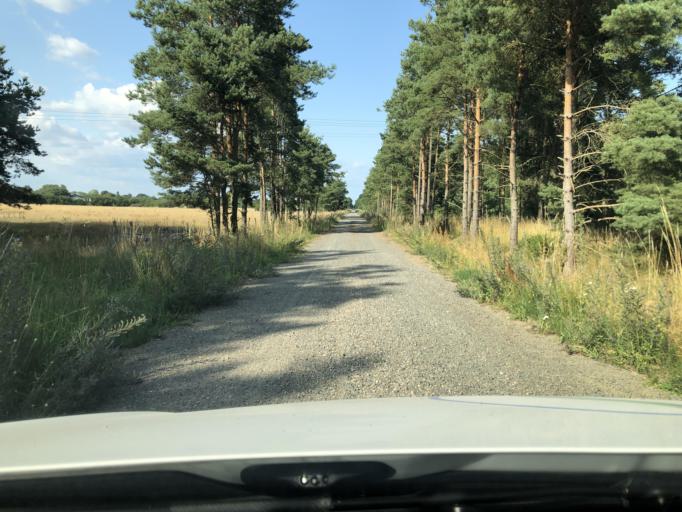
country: SE
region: Skane
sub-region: Kristianstads Kommun
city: Norra Asum
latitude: 55.9340
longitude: 14.1365
